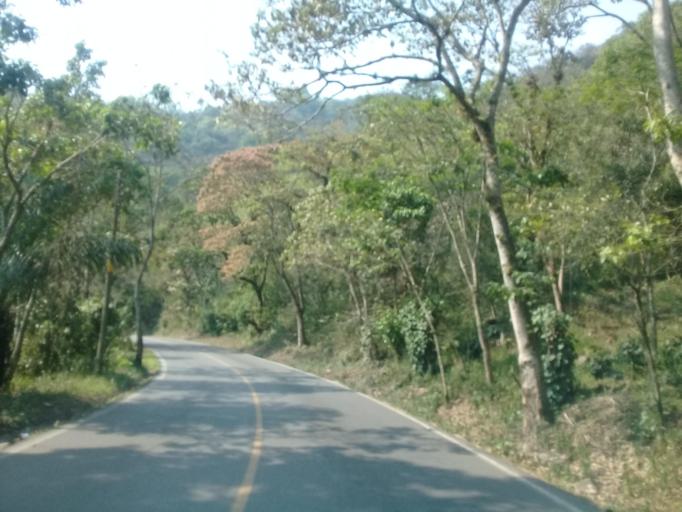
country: MX
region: Veracruz
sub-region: Ixtaczoquitlan
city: Campo Chico
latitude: 18.8406
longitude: -97.0233
